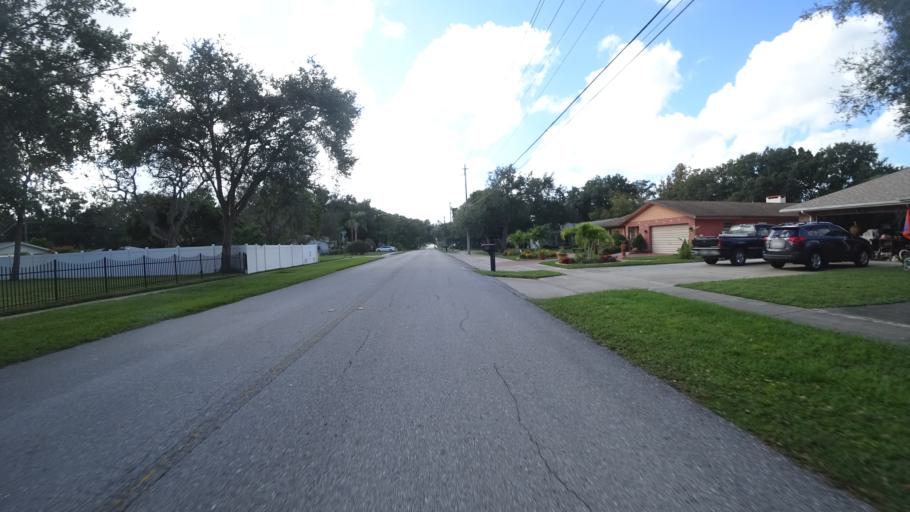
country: US
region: Florida
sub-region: Manatee County
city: West Bradenton
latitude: 27.5099
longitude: -82.6324
